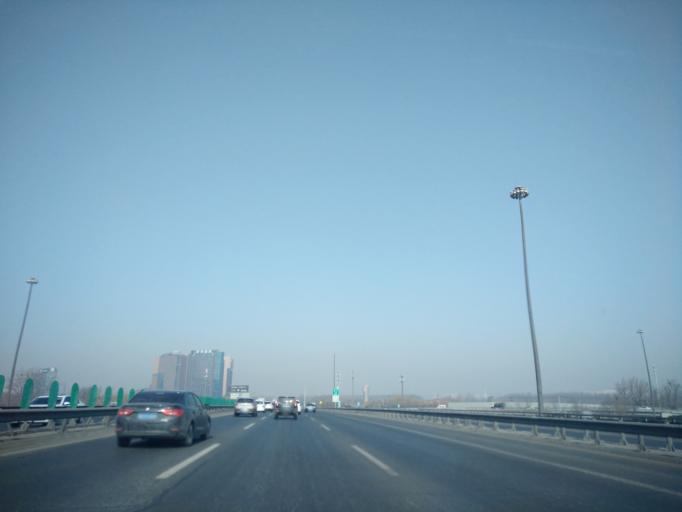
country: CN
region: Beijing
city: Wangjing
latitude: 39.9988
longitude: 116.4932
